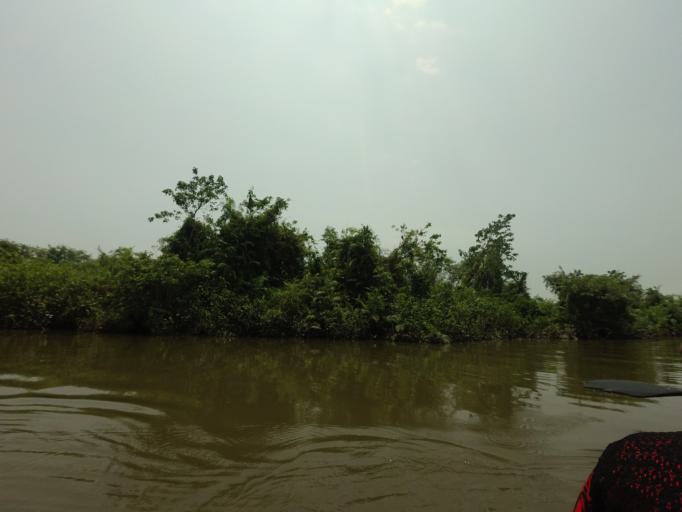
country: BD
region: Sylhet
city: Sylhet
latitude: 25.0124
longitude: 91.9160
